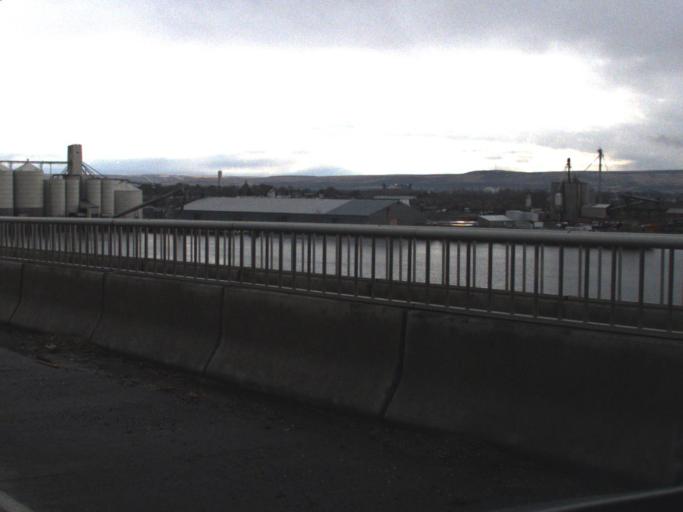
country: US
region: Washington
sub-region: Walla Walla County
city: Burbank
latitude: 46.2150
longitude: -119.0218
